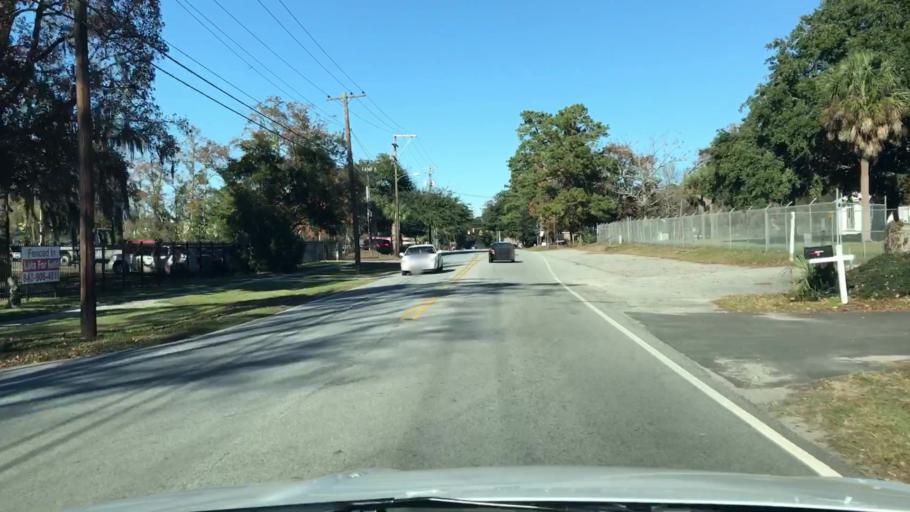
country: US
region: South Carolina
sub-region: Charleston County
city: North Charleston
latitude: 32.7981
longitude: -80.0157
